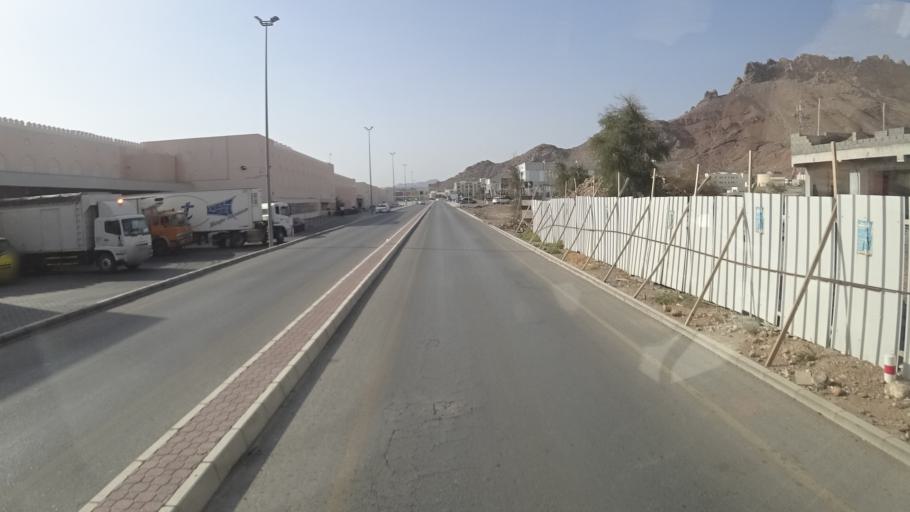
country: OM
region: Muhafazat ad Dakhiliyah
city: Nizwa
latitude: 22.8761
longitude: 57.5396
